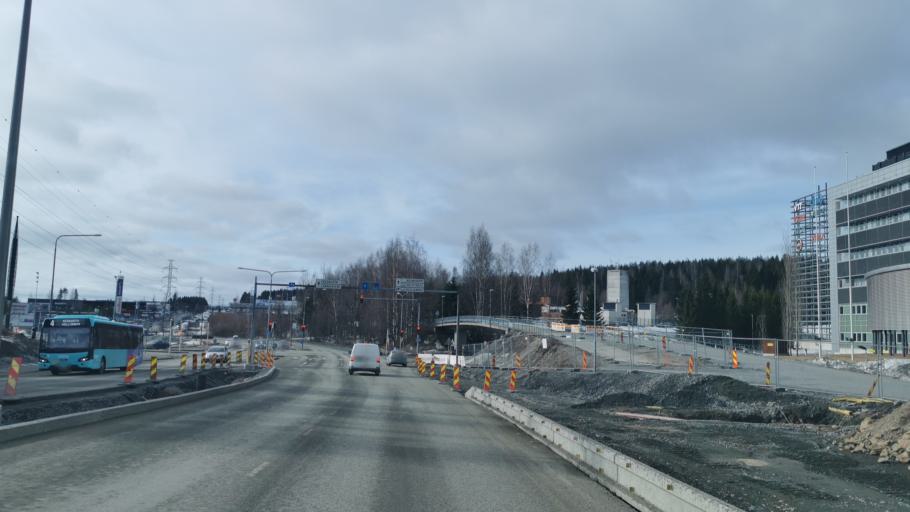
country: FI
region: Northern Savo
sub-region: Kuopio
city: Kuopio
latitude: 62.8879
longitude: 27.6304
